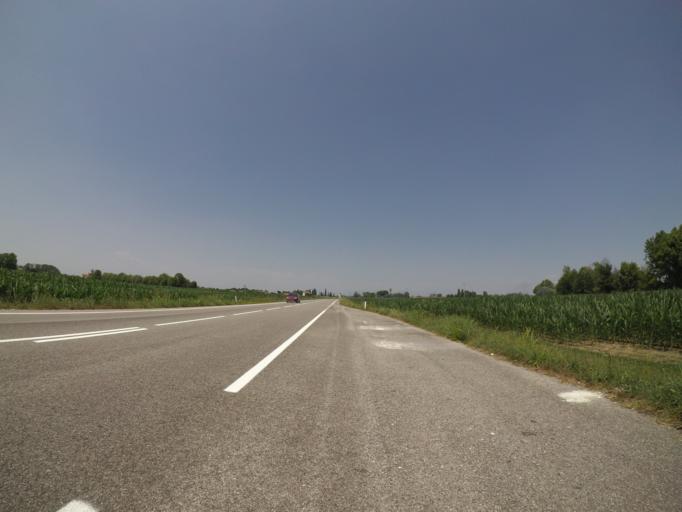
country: IT
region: Friuli Venezia Giulia
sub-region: Provincia di Udine
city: Varmo
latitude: 45.9001
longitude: 13.0060
